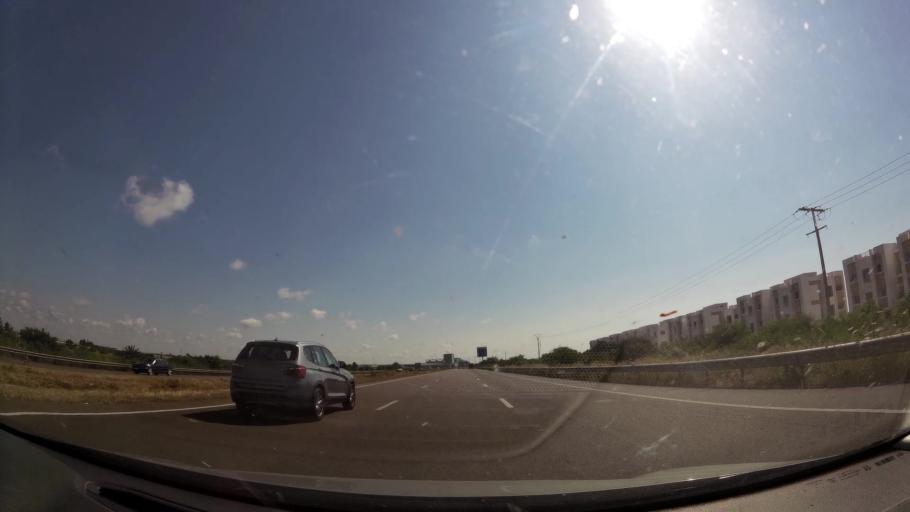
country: MA
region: Chaouia-Ouardigha
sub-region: Benslimane
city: Bouznika
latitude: 33.8085
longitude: -7.1429
